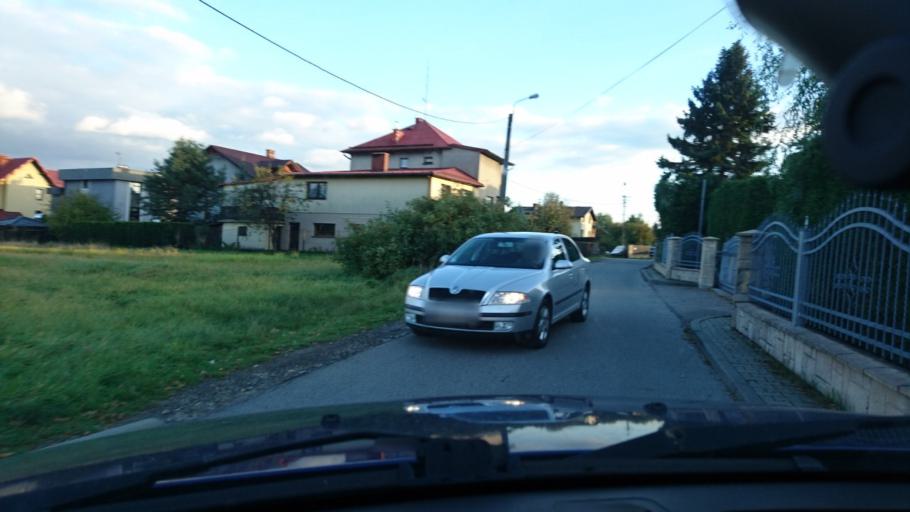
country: PL
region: Silesian Voivodeship
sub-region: Bielsko-Biala
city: Bielsko-Biala
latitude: 49.8422
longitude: 19.0643
